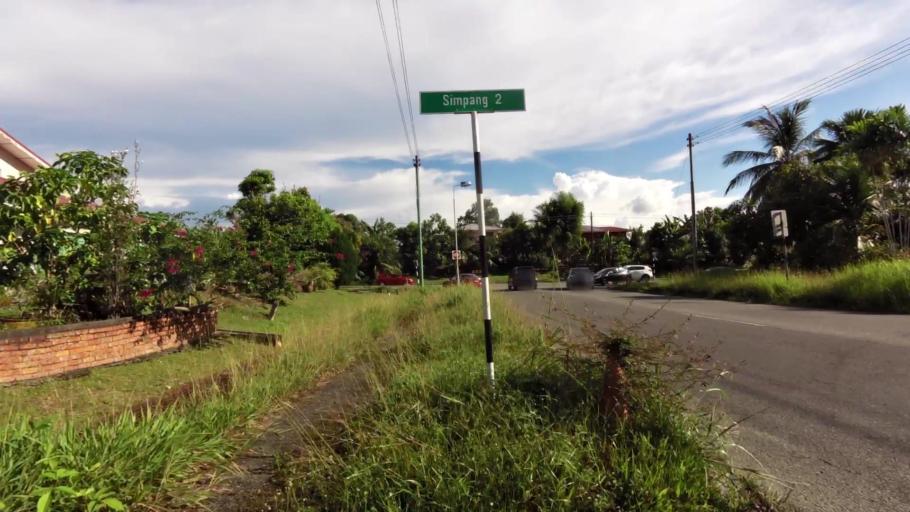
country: BN
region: Brunei and Muara
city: Bandar Seri Begawan
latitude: 4.9632
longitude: 114.9547
